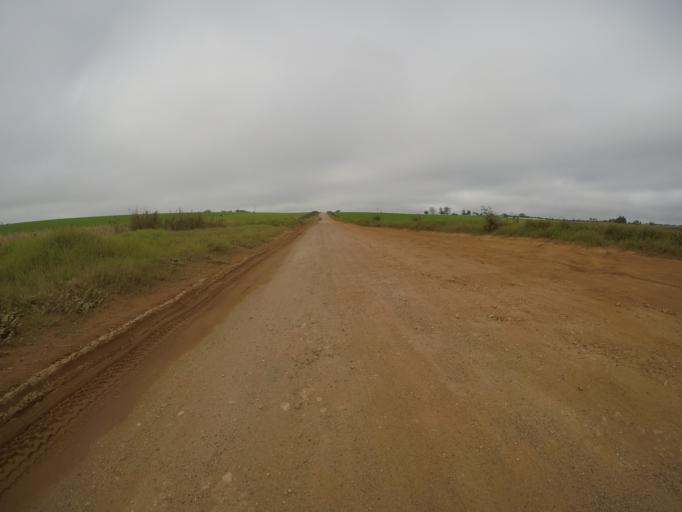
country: ZA
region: Eastern Cape
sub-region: Cacadu District Municipality
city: Kareedouw
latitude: -34.0273
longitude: 24.2425
